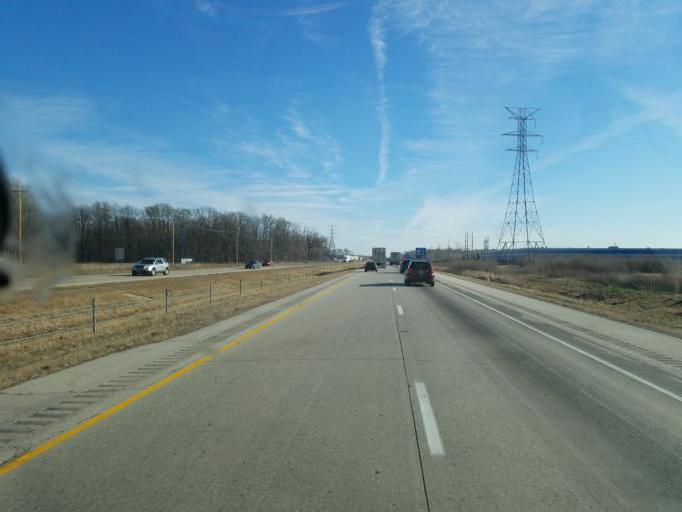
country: US
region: Indiana
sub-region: Hancock County
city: Greenfield
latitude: 39.8206
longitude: -85.7925
